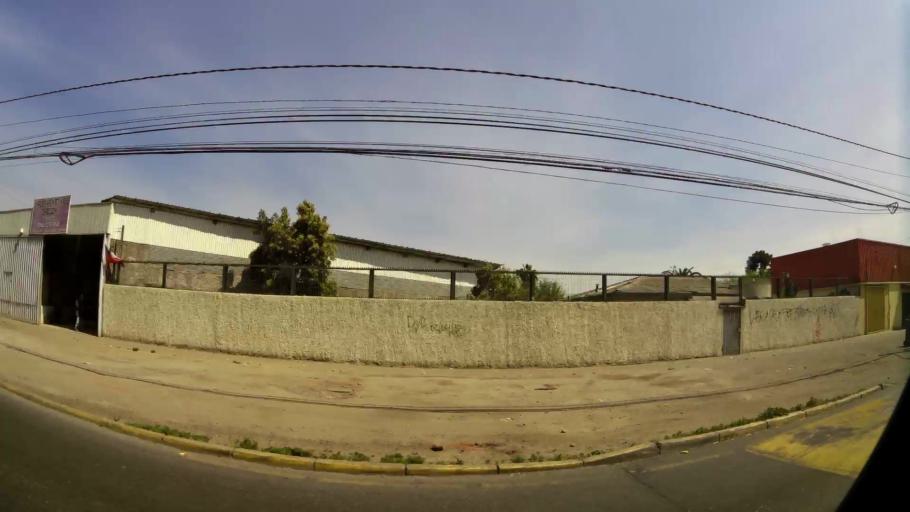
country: CL
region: Santiago Metropolitan
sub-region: Provincia de Santiago
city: Lo Prado
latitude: -33.4134
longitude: -70.7057
